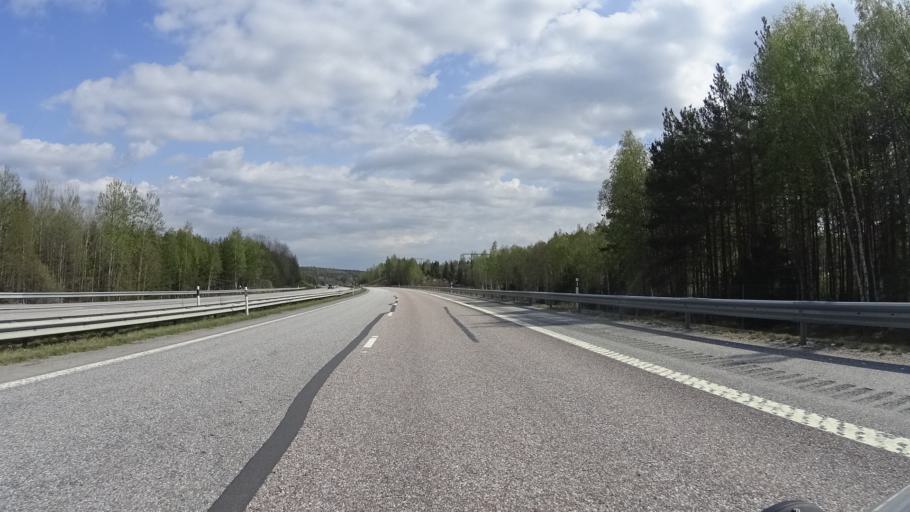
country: SE
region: Soedermanland
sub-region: Strangnas Kommun
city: Strangnas
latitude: 59.3685
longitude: 16.8531
